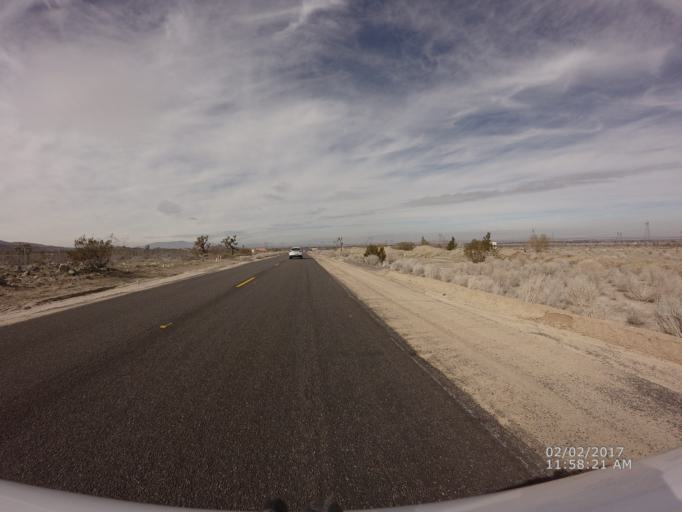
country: US
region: California
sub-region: Los Angeles County
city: Littlerock
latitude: 34.5042
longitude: -117.9642
